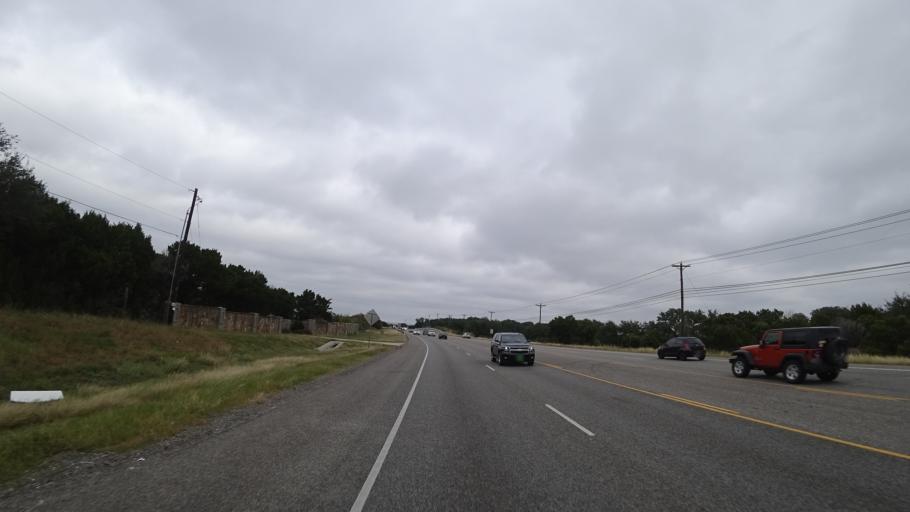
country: US
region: Texas
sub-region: Travis County
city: Bee Cave
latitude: 30.2869
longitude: -97.9168
